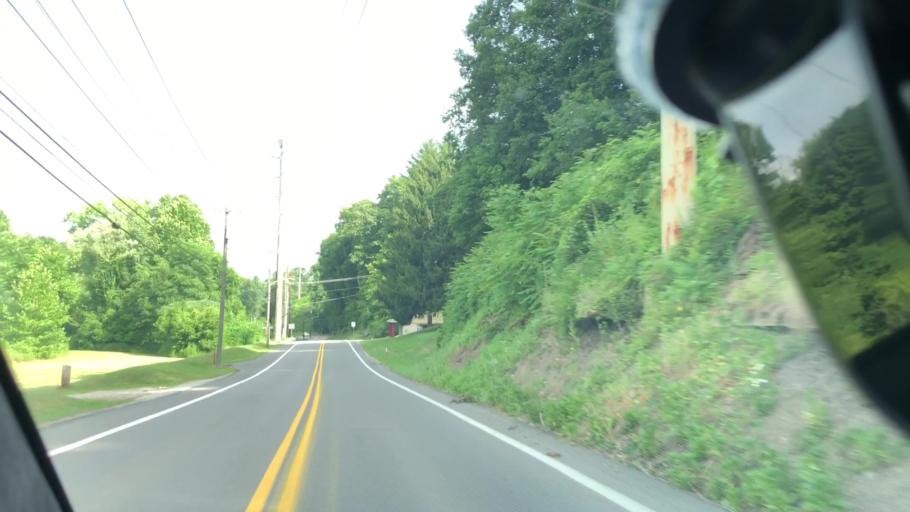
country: US
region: Pennsylvania
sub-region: Allegheny County
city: Upper Saint Clair
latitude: 40.3488
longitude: -80.0833
